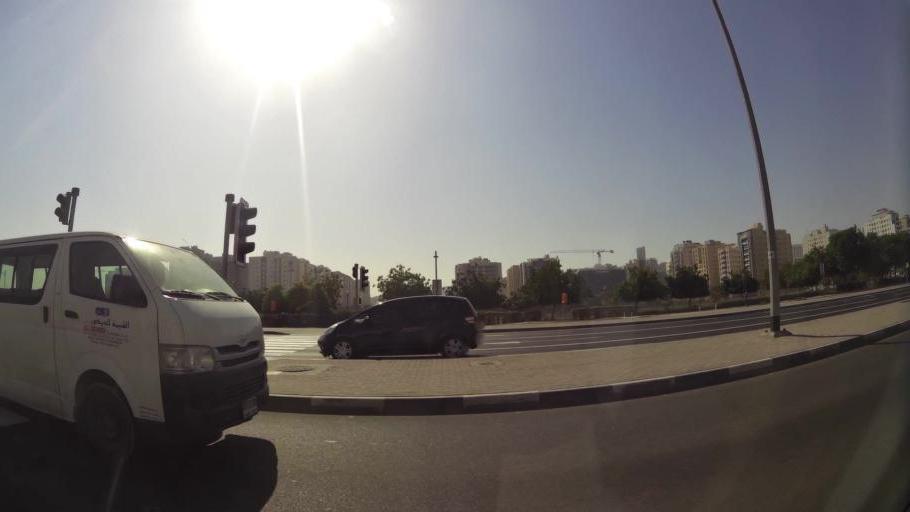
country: AE
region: Ash Shariqah
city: Sharjah
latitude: 25.2892
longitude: 55.3832
